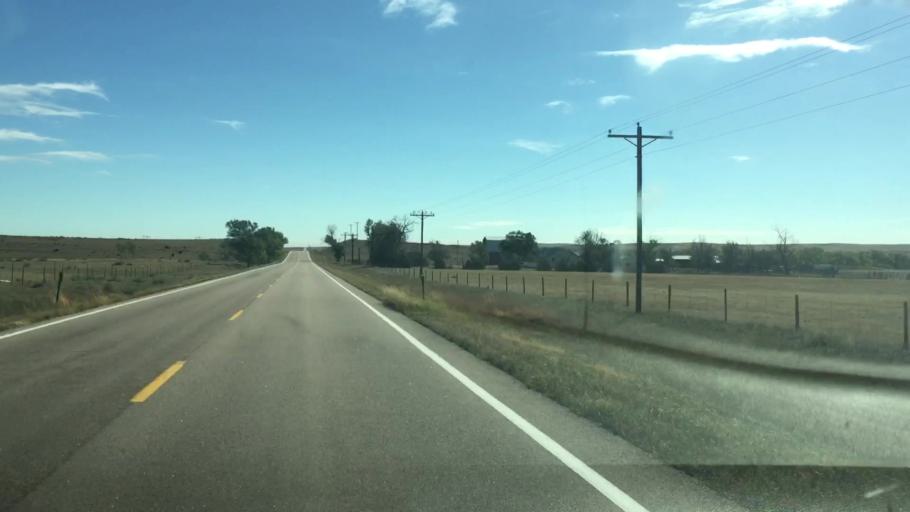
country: US
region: Colorado
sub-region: Elbert County
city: Kiowa
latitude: 39.2734
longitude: -104.1598
